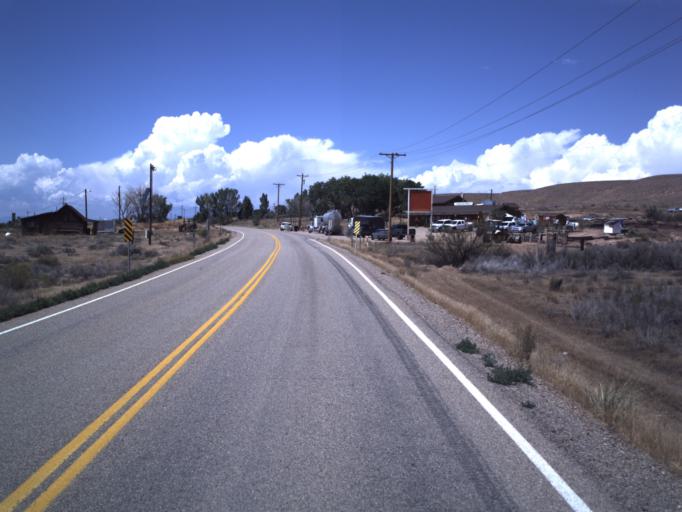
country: US
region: Utah
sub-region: Uintah County
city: Naples
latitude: 40.2103
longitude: -109.6679
